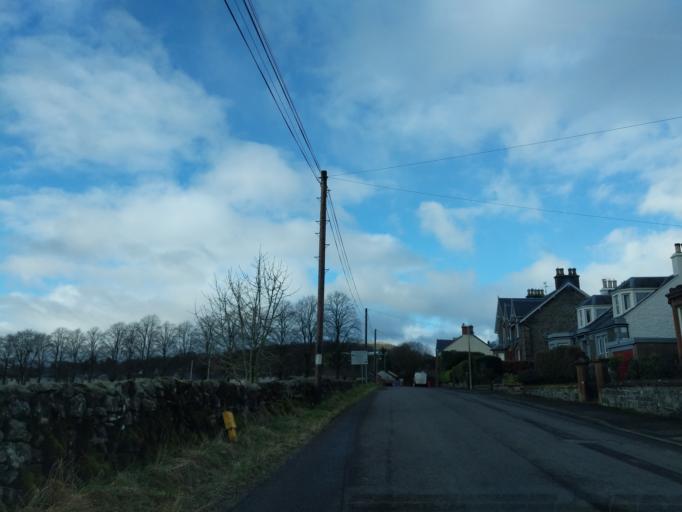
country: GB
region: Scotland
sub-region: Dumfries and Galloway
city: Moffat
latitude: 55.3299
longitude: -3.4333
